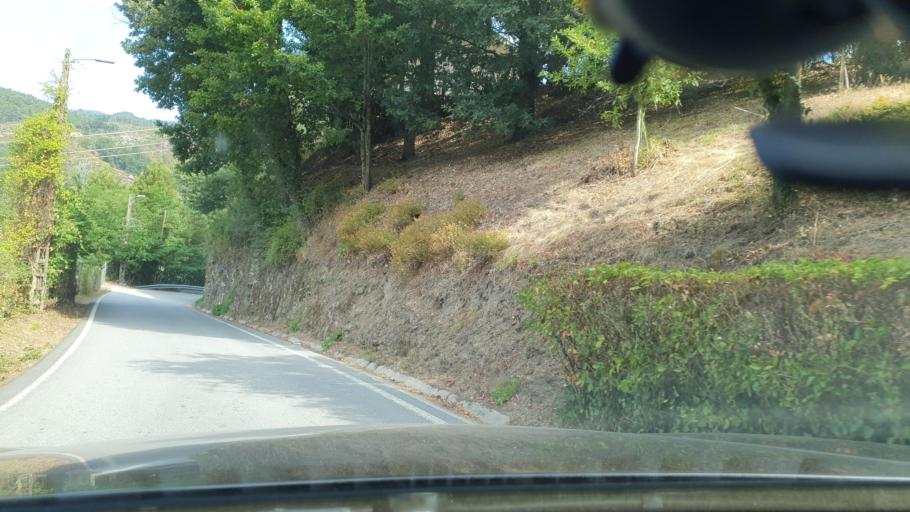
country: PT
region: Braga
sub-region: Vieira do Minho
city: Vieira do Minho
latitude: 41.6892
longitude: -8.0895
